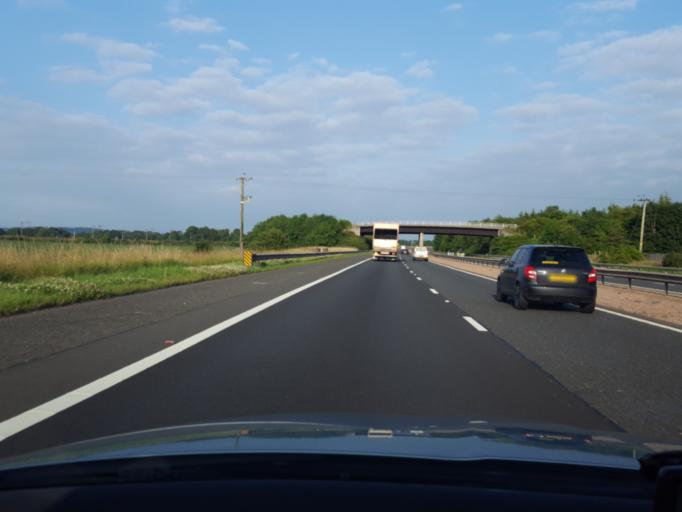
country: GB
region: Scotland
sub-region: Edinburgh
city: Ratho
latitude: 55.9306
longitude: -3.3683
